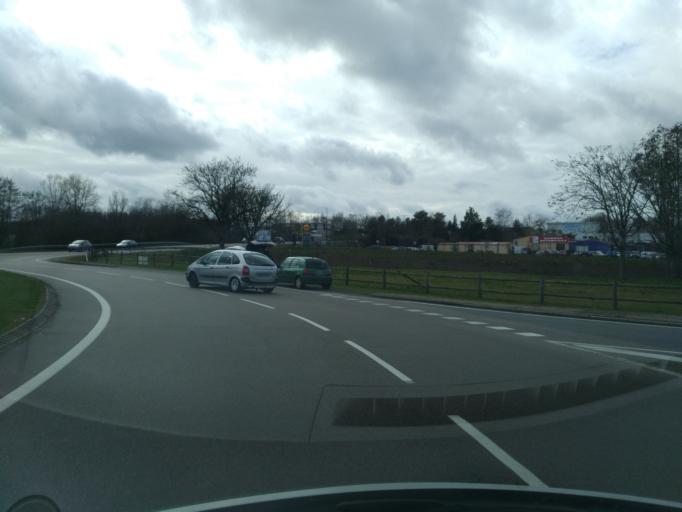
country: FR
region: Bourgogne
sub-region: Departement de Saone-et-Loire
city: Torcy
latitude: 46.7682
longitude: 4.4520
